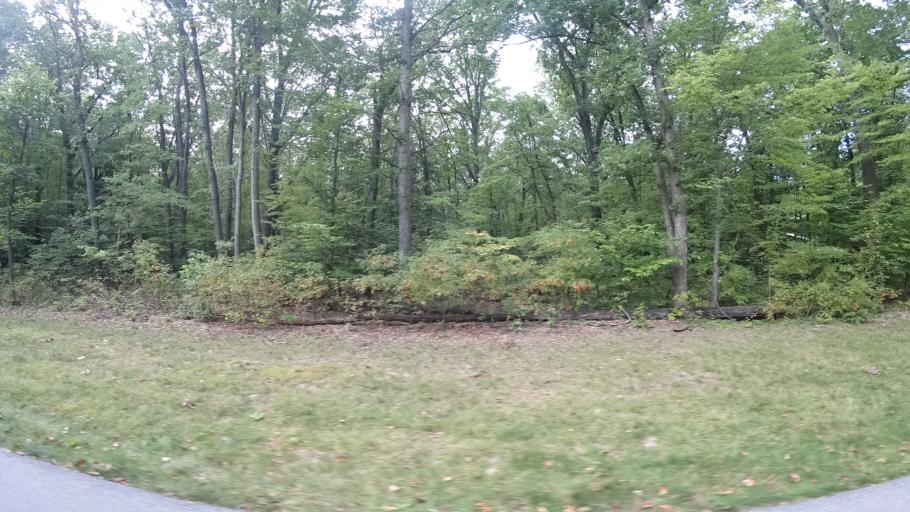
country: US
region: Indiana
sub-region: LaPorte County
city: Long Beach
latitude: 41.7273
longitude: -86.8506
